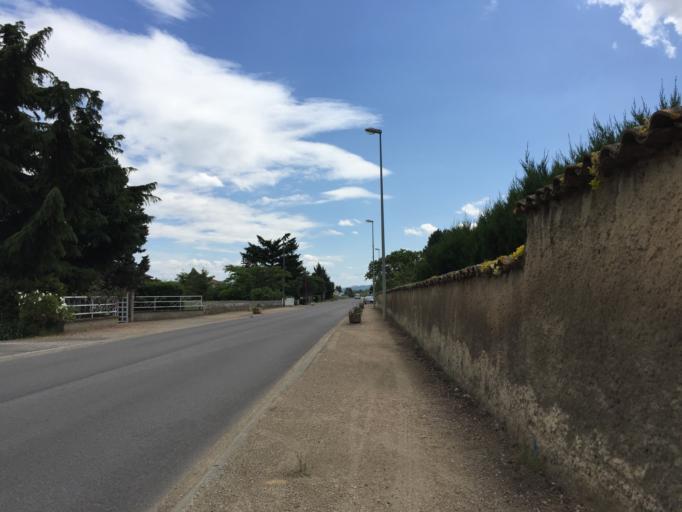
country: FR
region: Rhone-Alpes
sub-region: Departement de la Drome
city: Andancette
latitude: 45.2695
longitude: 4.8005
